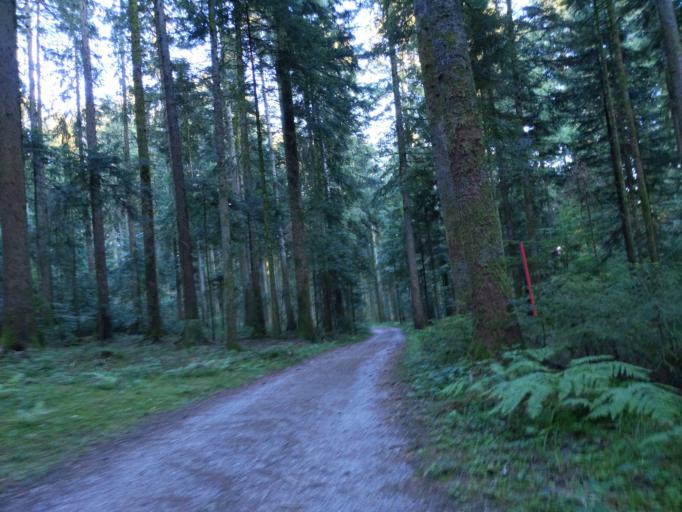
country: DE
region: Baden-Wuerttemberg
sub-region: Karlsruhe Region
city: Alpirsbach
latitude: 48.3372
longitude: 8.4118
